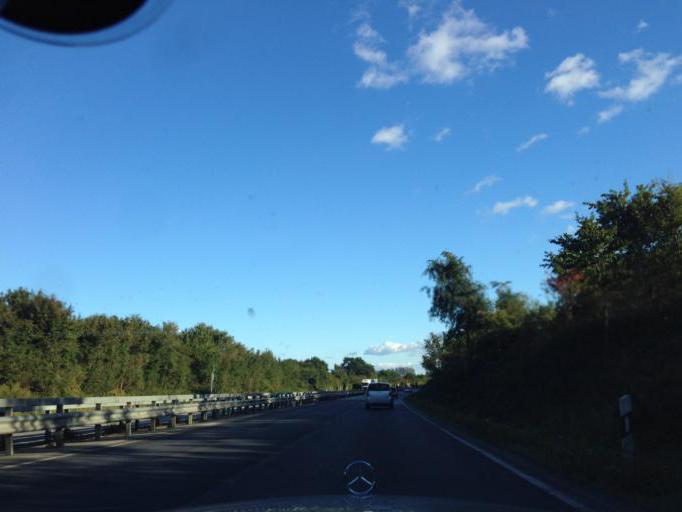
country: DE
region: Schleswig-Holstein
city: Schackendorf
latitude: 53.9540
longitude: 10.2702
